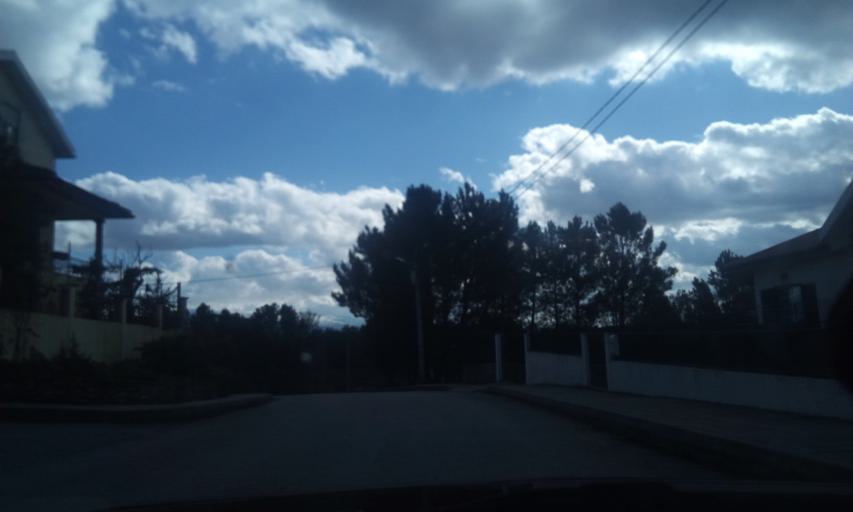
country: PT
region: Guarda
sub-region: Fornos de Algodres
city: Fornos de Algodres
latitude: 40.6276
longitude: -7.5422
